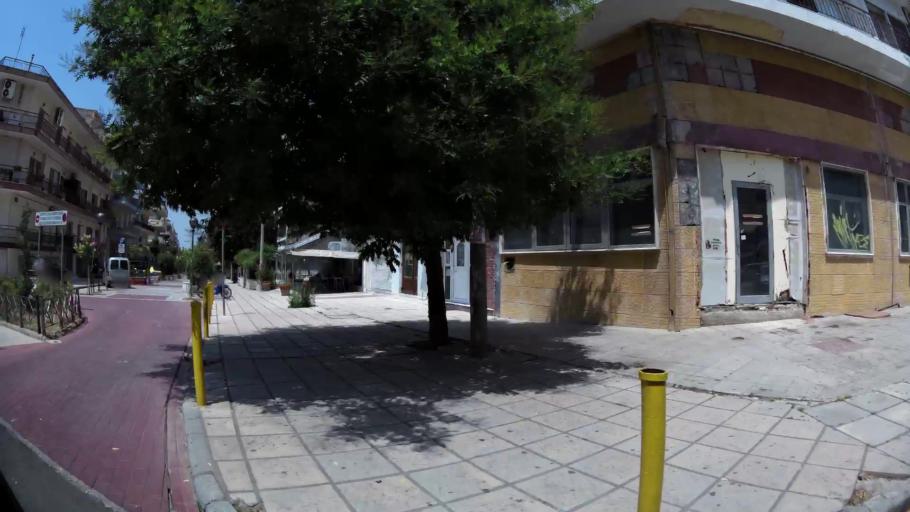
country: GR
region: Central Macedonia
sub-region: Nomos Thessalonikis
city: Evosmos
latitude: 40.6699
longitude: 22.8980
